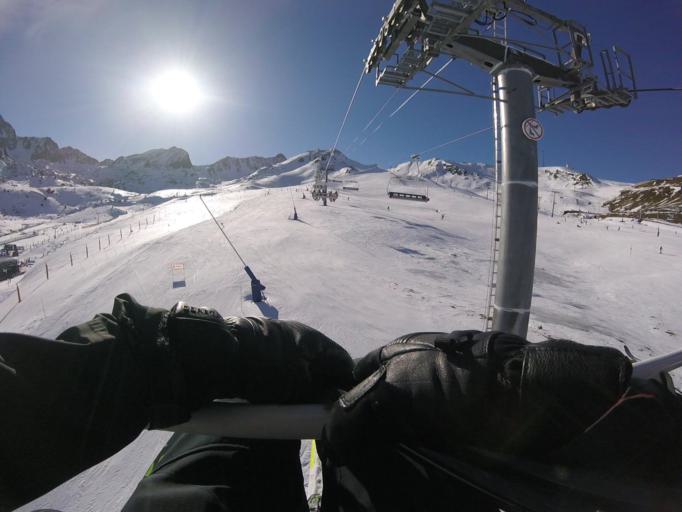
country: AD
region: Encamp
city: Pas de la Casa
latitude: 42.5381
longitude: 1.7321
